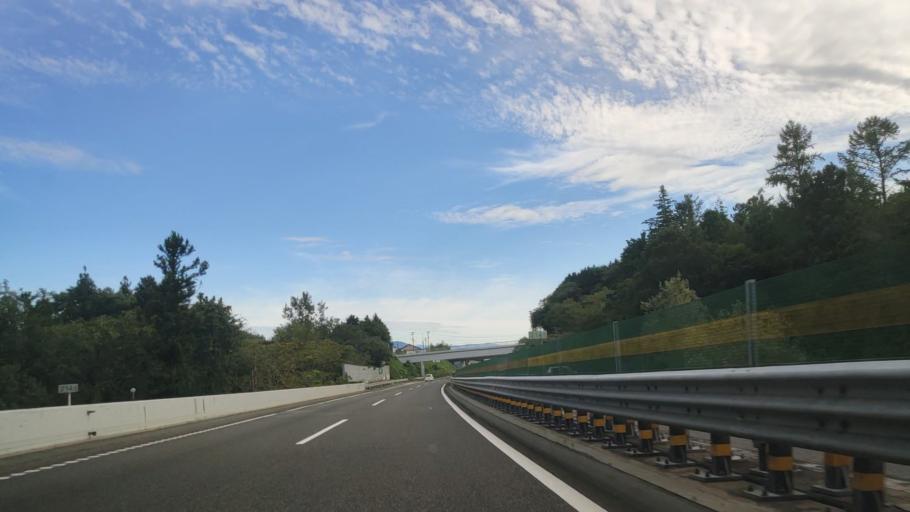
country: JP
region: Nagano
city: Ina
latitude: 35.7894
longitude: 137.9345
